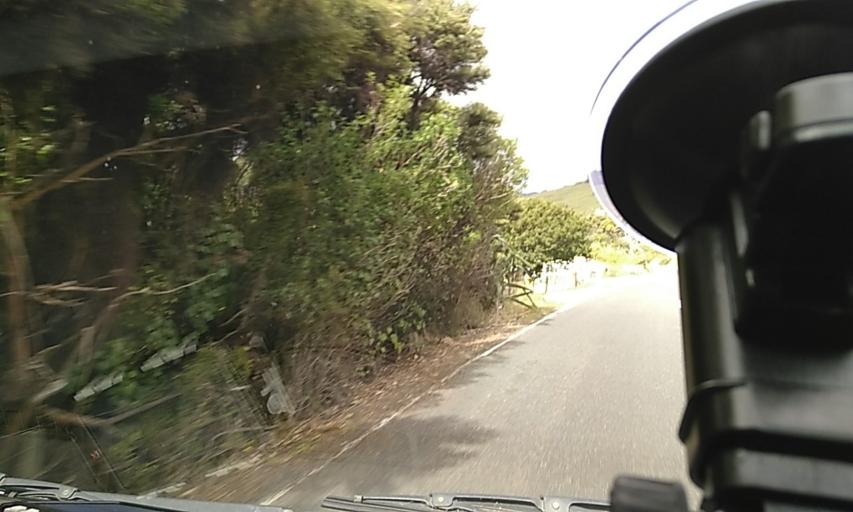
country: NZ
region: Northland
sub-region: Far North District
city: Ahipara
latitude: -35.5380
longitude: 173.3814
